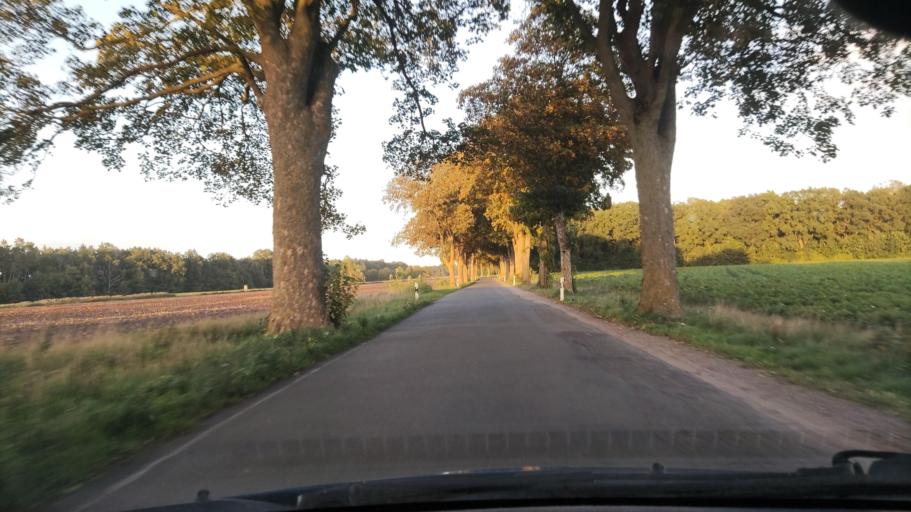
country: DE
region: Mecklenburg-Vorpommern
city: Lubtheen
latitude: 53.3197
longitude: 11.0353
